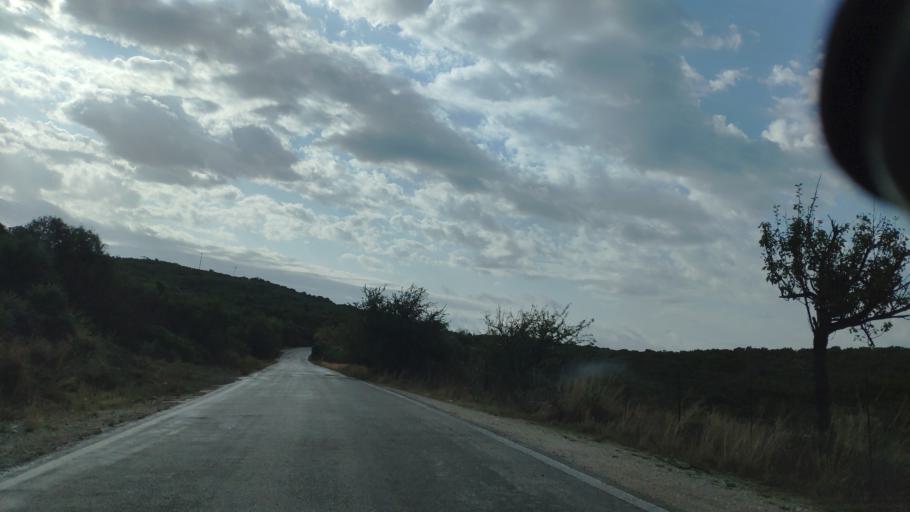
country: GR
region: West Greece
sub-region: Nomos Aitolias kai Akarnanias
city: Sardinia
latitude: 38.8820
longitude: 21.2459
